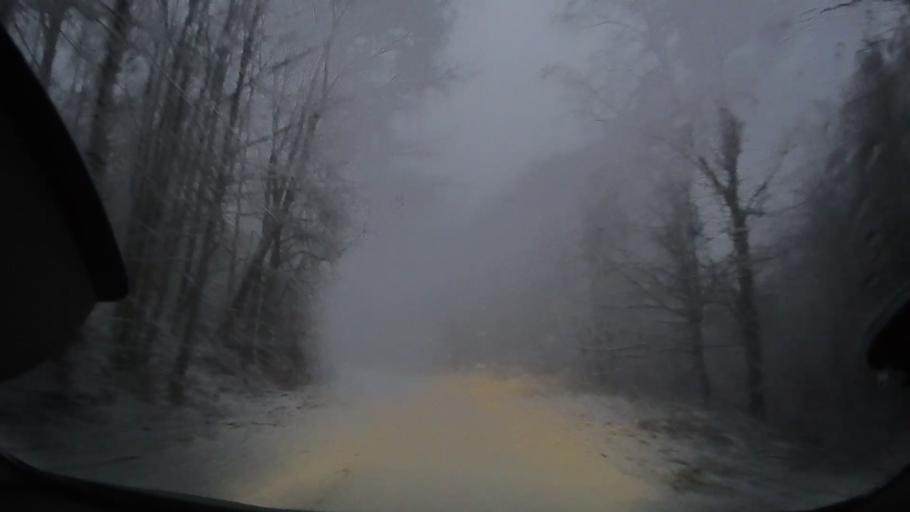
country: RO
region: Alba
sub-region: Comuna Avram Iancu
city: Avram Iancu
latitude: 46.3122
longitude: 22.8060
